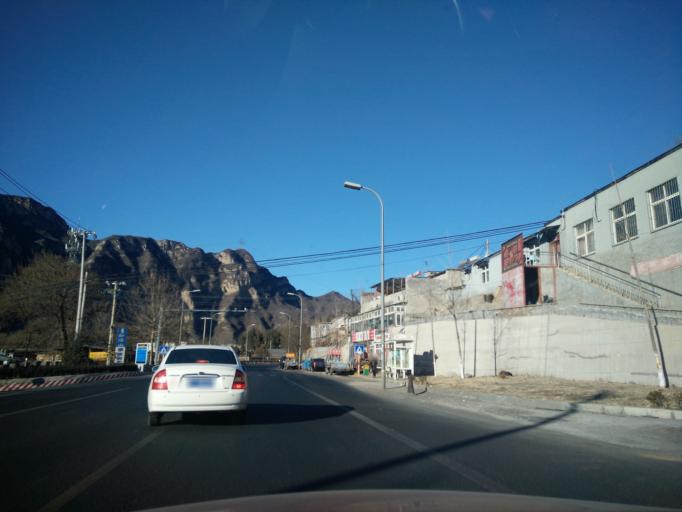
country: CN
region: Beijing
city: Miaofengshan
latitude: 39.9757
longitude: 116.0447
